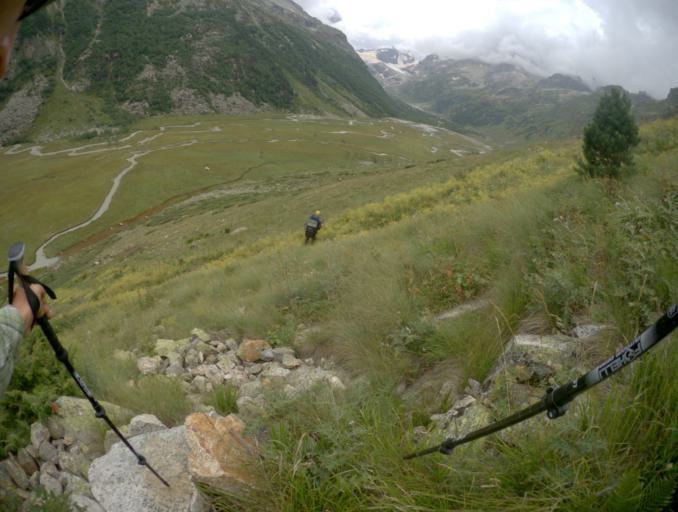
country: RU
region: Karachayevo-Cherkesiya
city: Uchkulan
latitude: 43.2675
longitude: 42.1393
